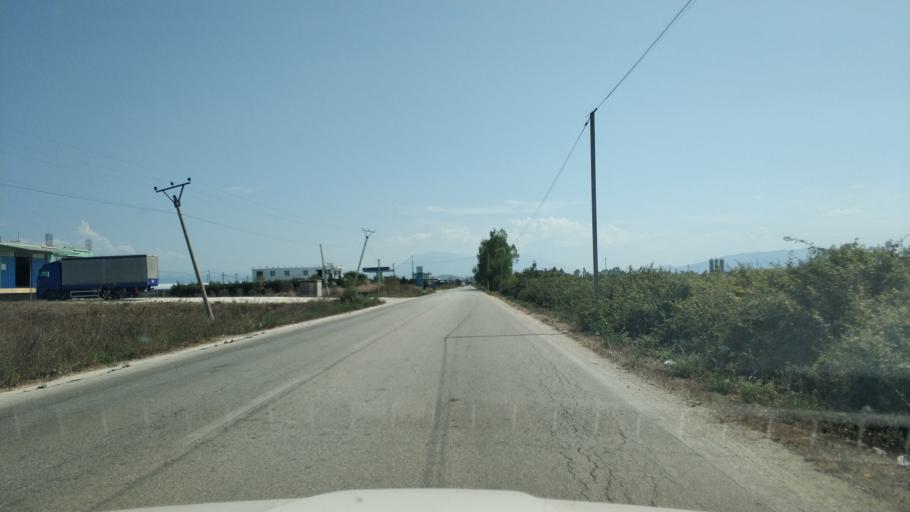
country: AL
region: Fier
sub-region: Rrethi i Lushnjes
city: Krutja e Poshtme
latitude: 40.8825
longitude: 19.6603
